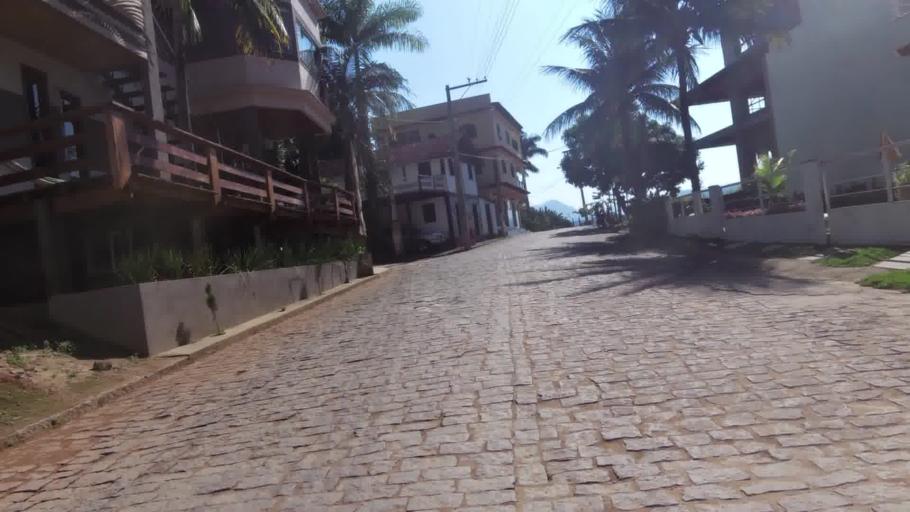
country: BR
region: Espirito Santo
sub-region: Alfredo Chaves
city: Alfredo Chaves
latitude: -20.6794
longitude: -40.7723
